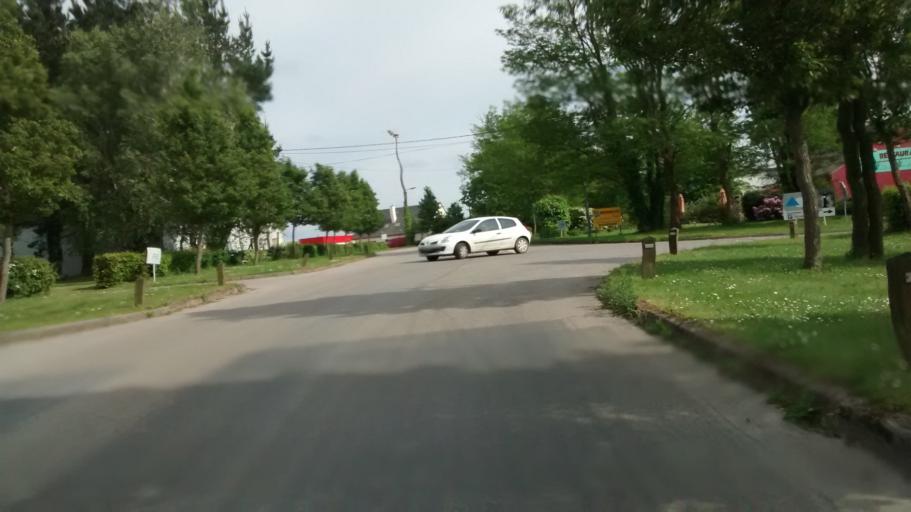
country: FR
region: Brittany
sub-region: Departement du Morbihan
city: Malestroit
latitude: 47.8022
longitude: -2.4010
